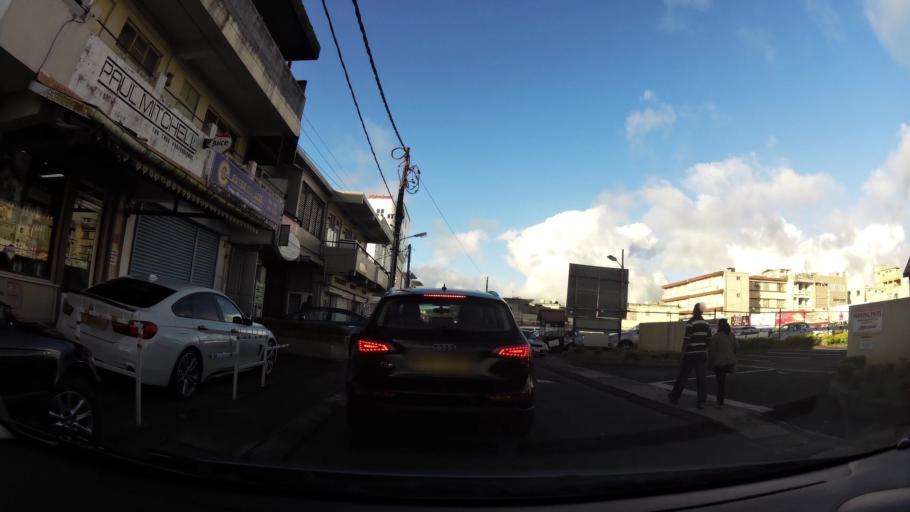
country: MU
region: Plaines Wilhems
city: Curepipe
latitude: -20.3166
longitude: 57.5224
